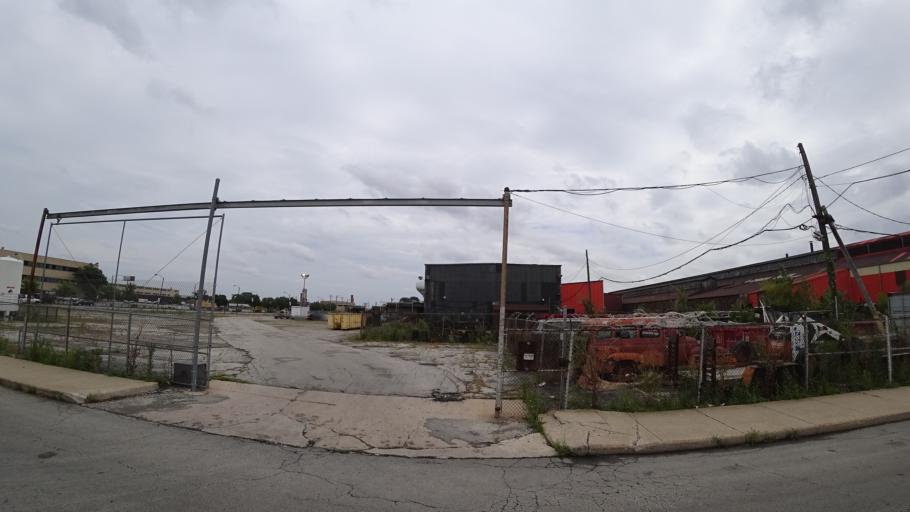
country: US
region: Illinois
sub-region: Cook County
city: Cicero
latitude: 41.8649
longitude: -87.7594
